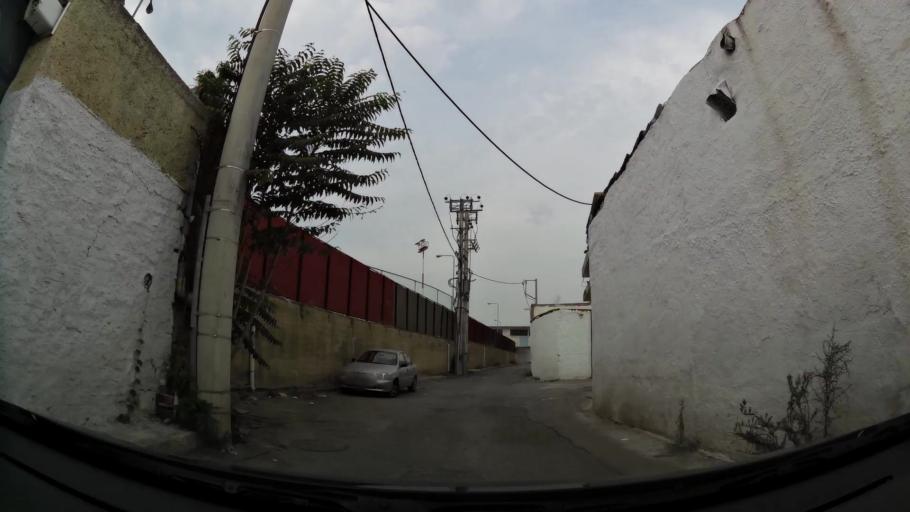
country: GR
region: Attica
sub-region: Nomarchia Athinas
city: Tavros
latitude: 37.9724
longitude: 23.6847
